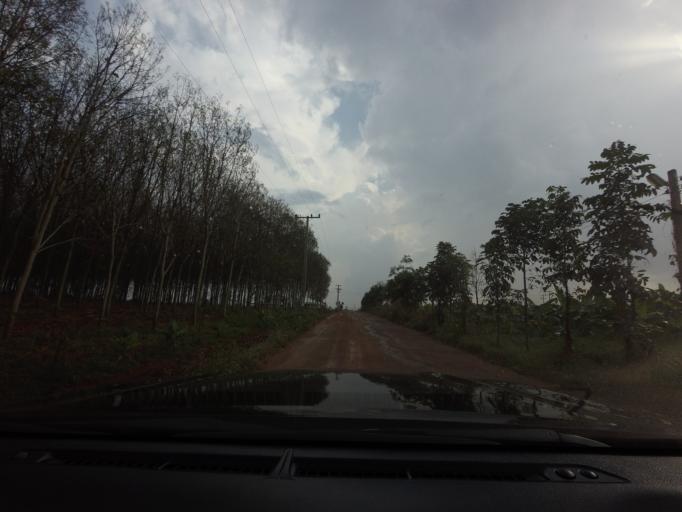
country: TH
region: Nakhon Ratchasima
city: Wang Nam Khiao
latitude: 14.4110
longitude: 101.7389
